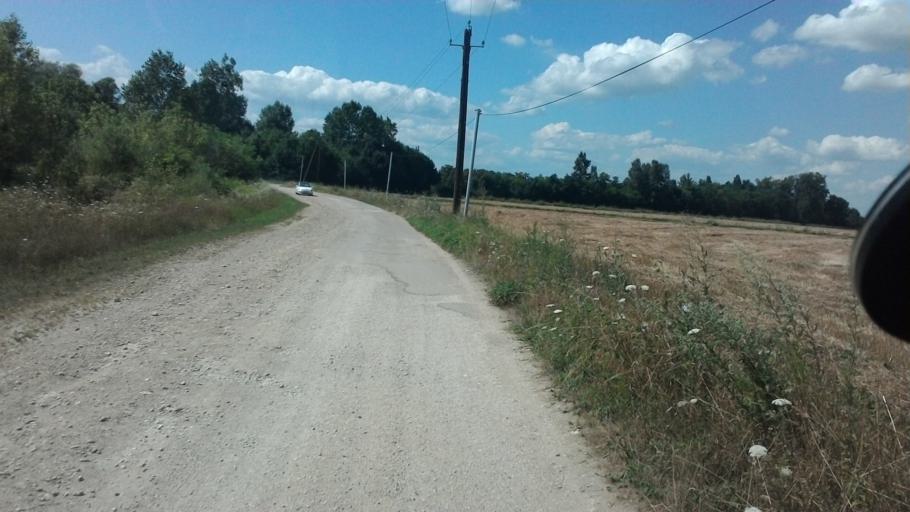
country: FR
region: Bourgogne
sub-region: Departement de la Cote-d'Or
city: Seurre
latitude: 46.9386
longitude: 5.1539
